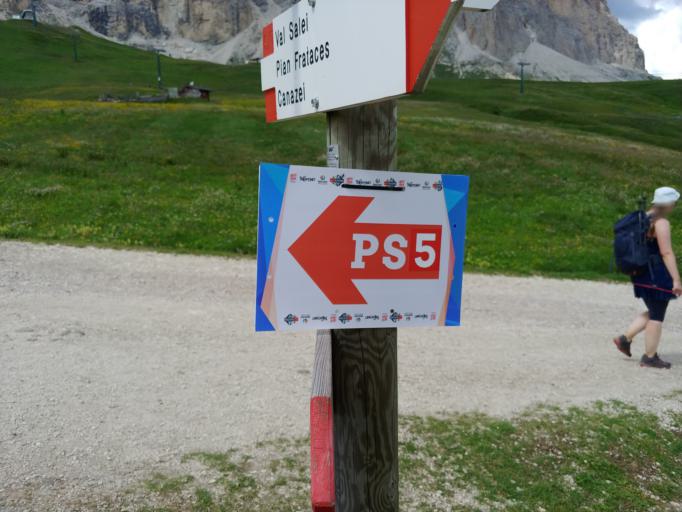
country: IT
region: Trentino-Alto Adige
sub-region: Provincia di Trento
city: Campitello di Fassa
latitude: 46.5027
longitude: 11.7513
